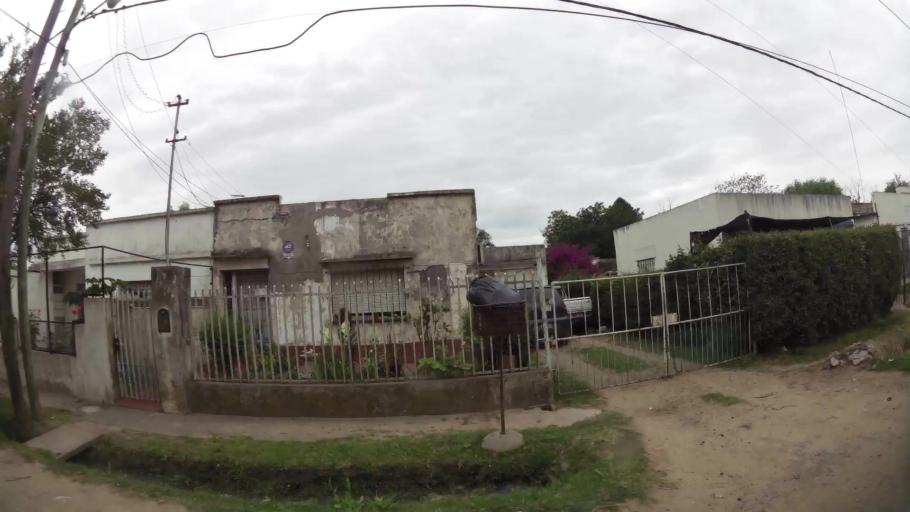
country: AR
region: Buenos Aires
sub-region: Partido de Zarate
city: Zarate
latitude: -34.1173
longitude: -59.0318
